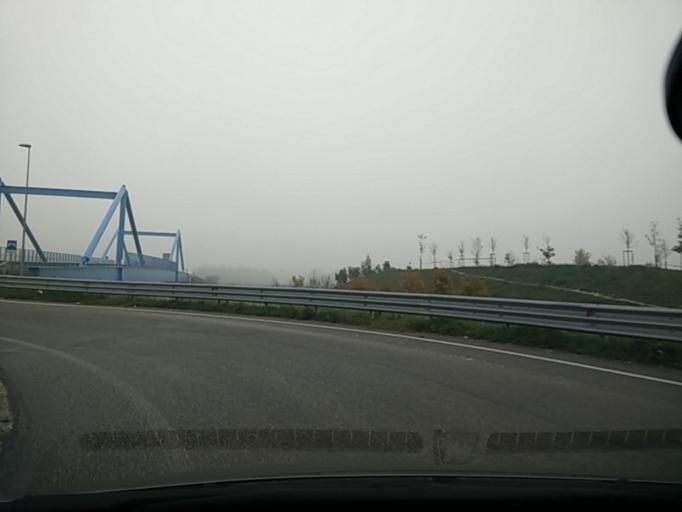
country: IT
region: Veneto
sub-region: Provincia di Venezia
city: Martellago
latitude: 45.5430
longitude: 12.1440
